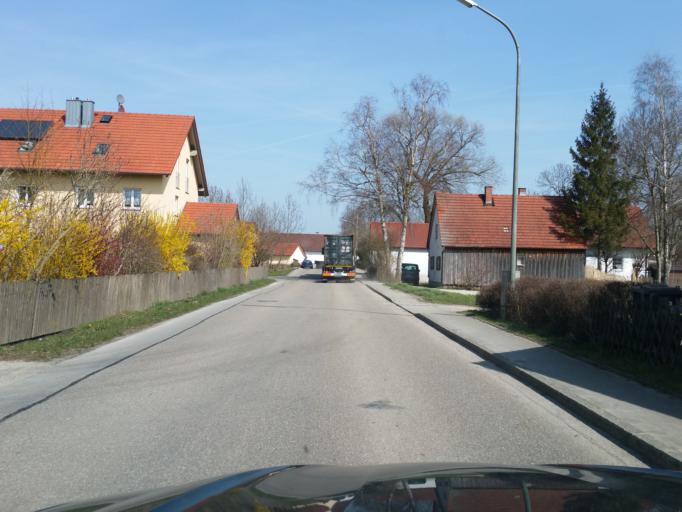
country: DE
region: Bavaria
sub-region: Upper Bavaria
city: Berglern
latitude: 48.3948
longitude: 11.9198
